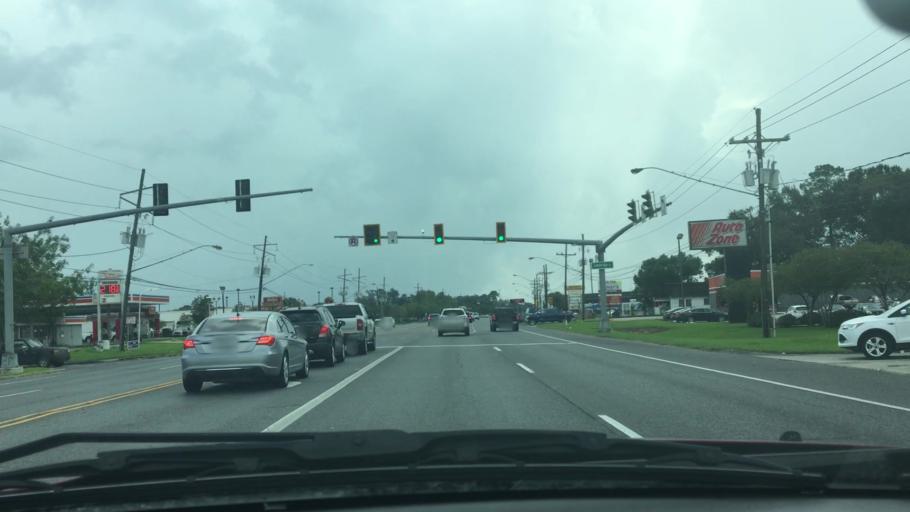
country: US
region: Louisiana
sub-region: Saint John the Baptist Parish
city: Laplace
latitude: 30.0701
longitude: -90.4871
